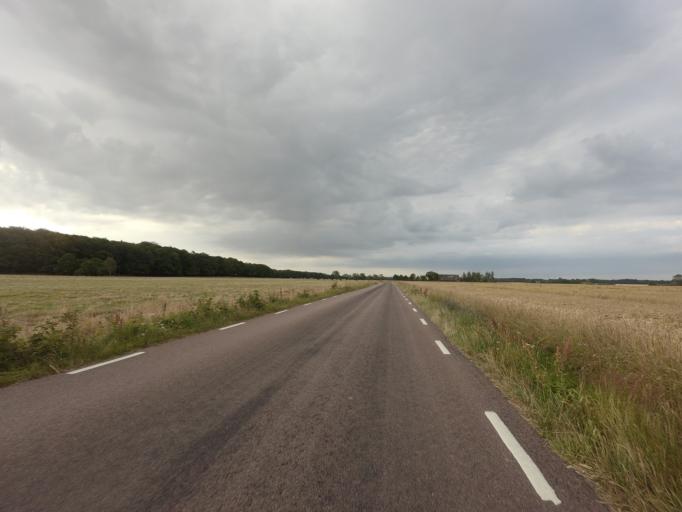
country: SE
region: Skane
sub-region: Helsingborg
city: Odakra
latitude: 56.1519
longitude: 12.7311
